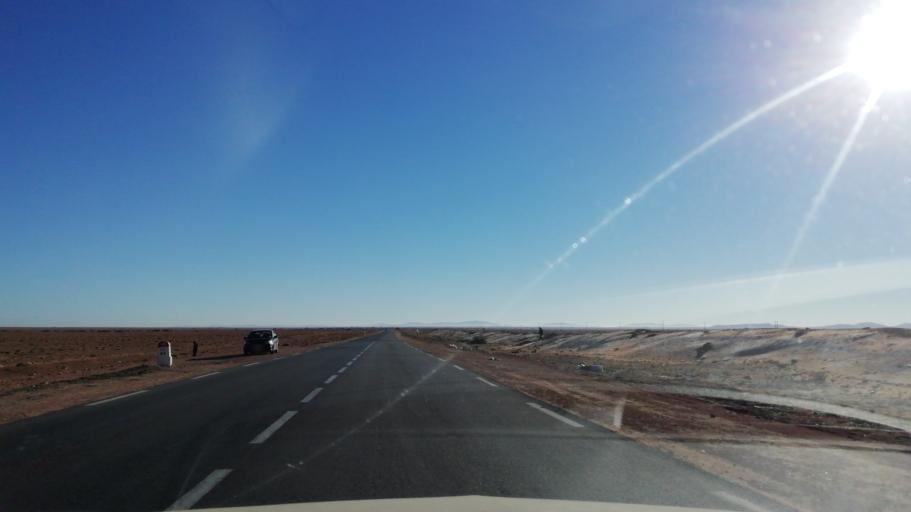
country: DZ
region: El Bayadh
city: El Bayadh
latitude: 33.8585
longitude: 0.5718
